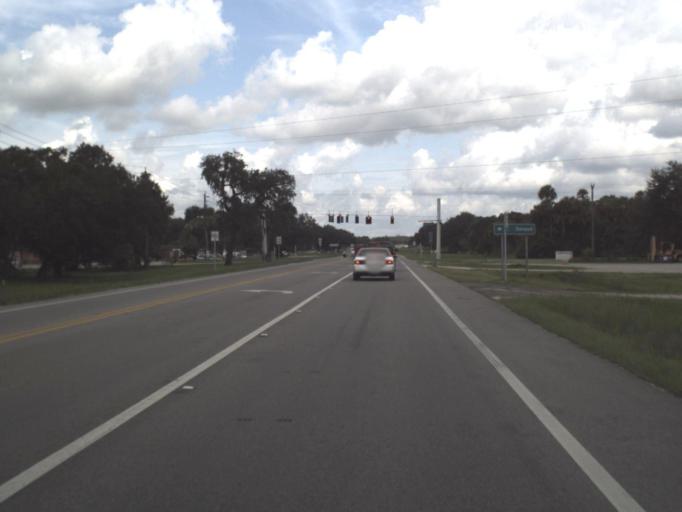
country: US
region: Florida
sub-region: Hendry County
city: LaBelle
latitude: 26.7746
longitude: -81.4374
